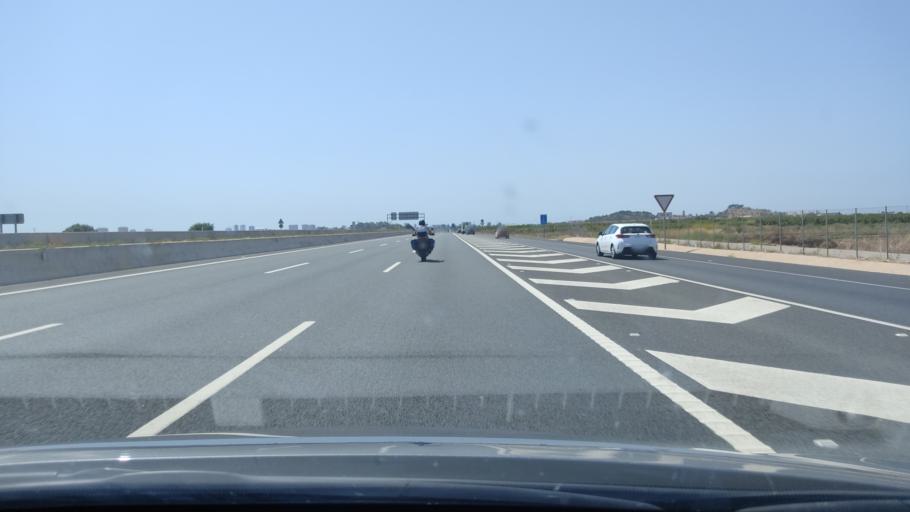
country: ES
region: Valencia
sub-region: Provincia de Valencia
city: Pucol
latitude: 39.6133
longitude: -0.2946
